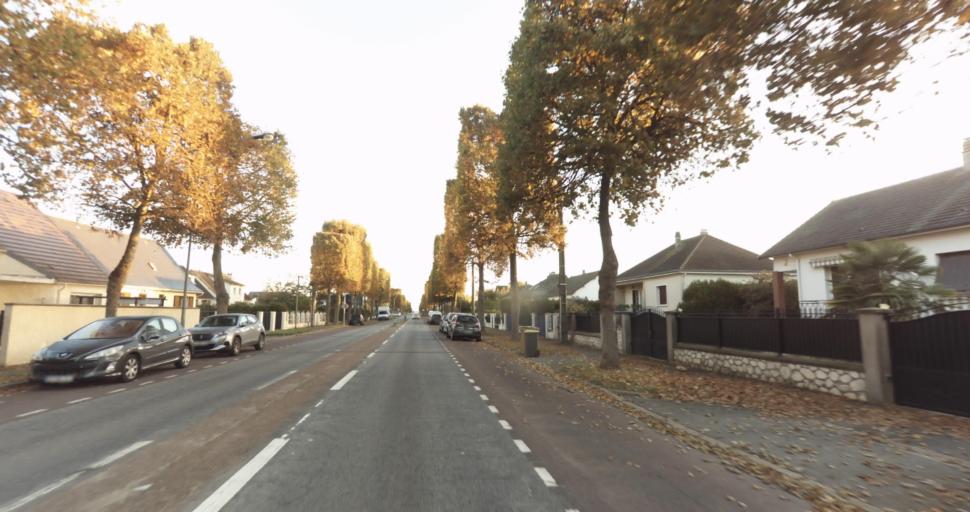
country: FR
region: Centre
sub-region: Departement d'Eure-et-Loir
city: Vernouillet
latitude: 48.7133
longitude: 1.3612
